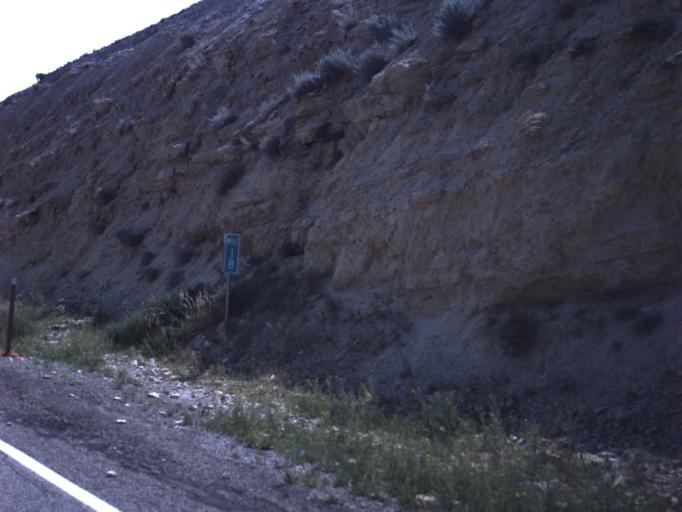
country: US
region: Utah
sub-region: Daggett County
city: Manila
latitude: 40.9104
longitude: -109.6979
